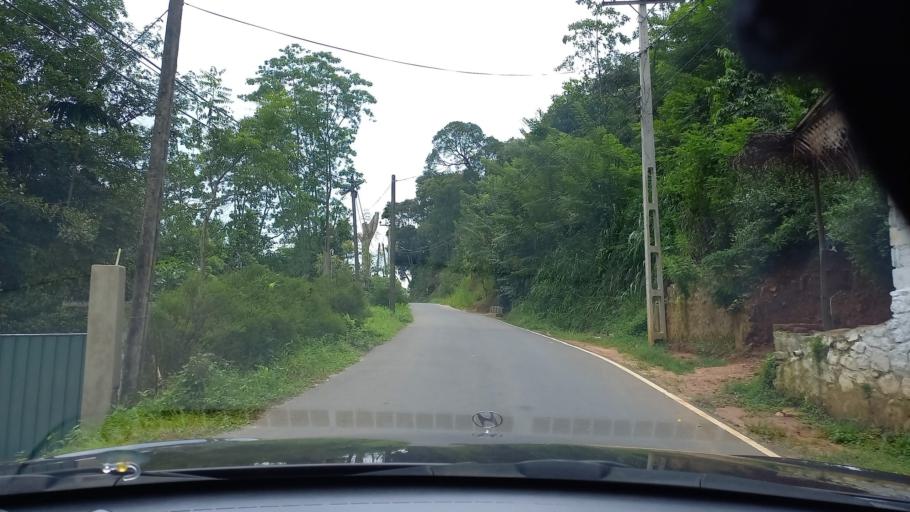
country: LK
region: Central
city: Gampola
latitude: 7.2205
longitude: 80.6113
